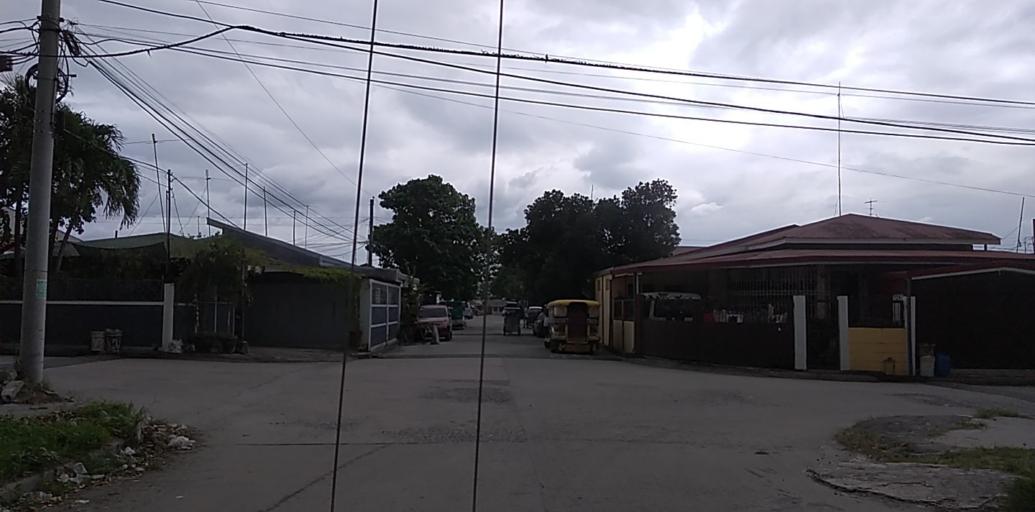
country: PH
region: Central Luzon
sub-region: Province of Pampanga
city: Pio
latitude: 15.0432
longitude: 120.5298
